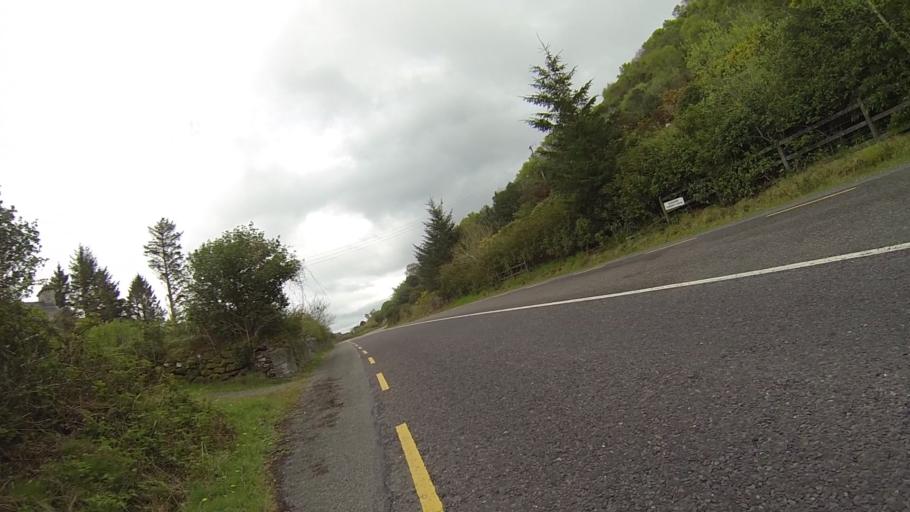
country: IE
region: Munster
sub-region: County Cork
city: Bantry
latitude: 51.7192
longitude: -9.5795
